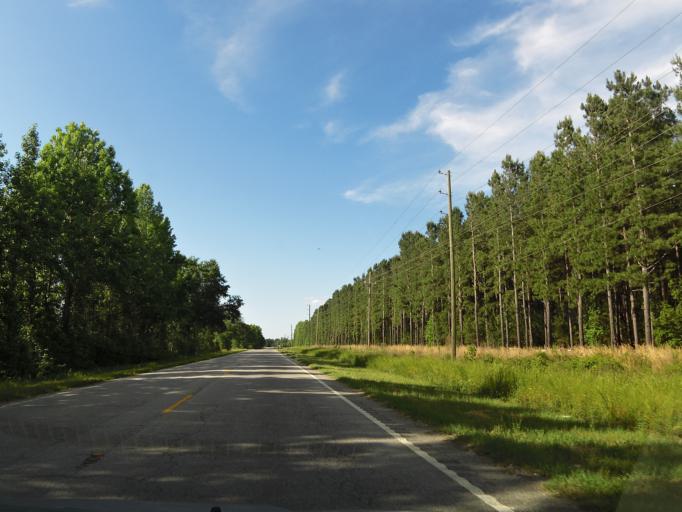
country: US
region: South Carolina
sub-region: Allendale County
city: Fairfax
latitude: 32.9295
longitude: -81.2372
